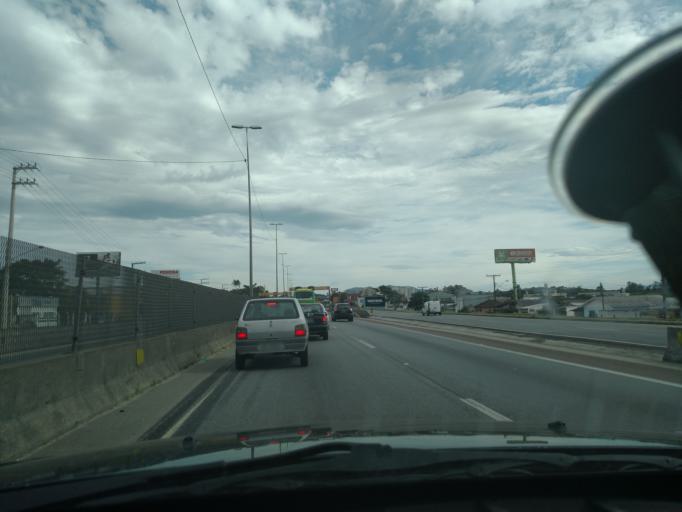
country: BR
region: Santa Catarina
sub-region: Sao Jose
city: Campinas
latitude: -27.5604
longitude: -48.6171
